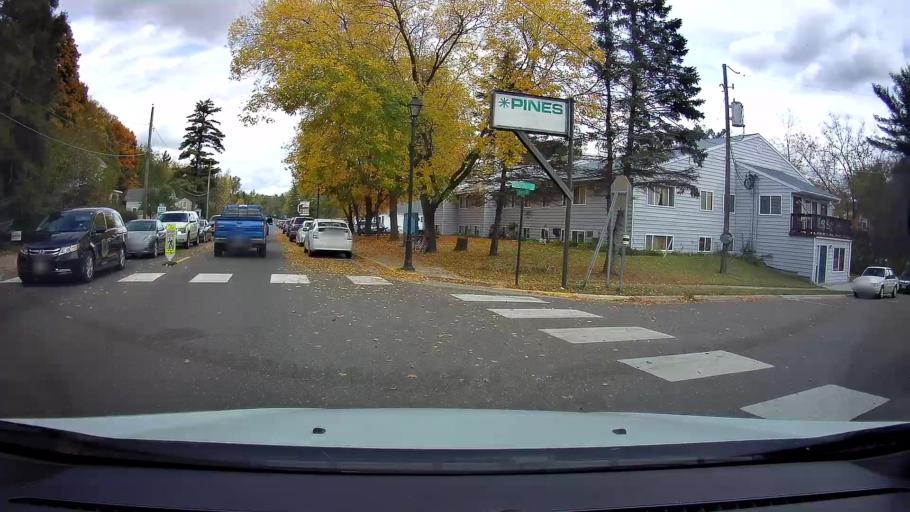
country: US
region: Wisconsin
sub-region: Polk County
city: Saint Croix Falls
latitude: 45.4045
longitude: -92.6526
